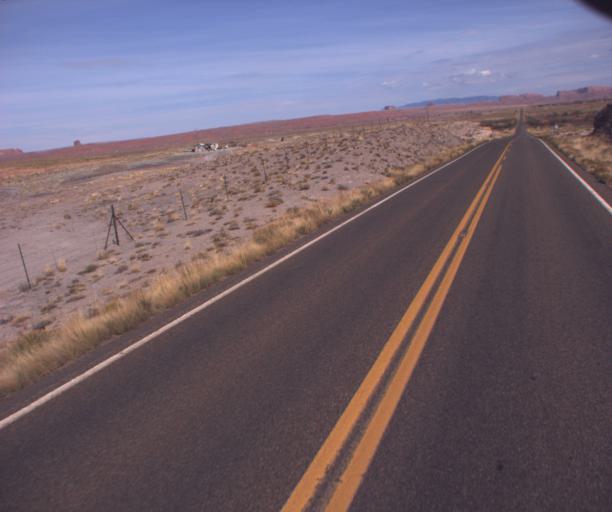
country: US
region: Arizona
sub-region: Apache County
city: Many Farms
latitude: 36.4889
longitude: -109.4987
